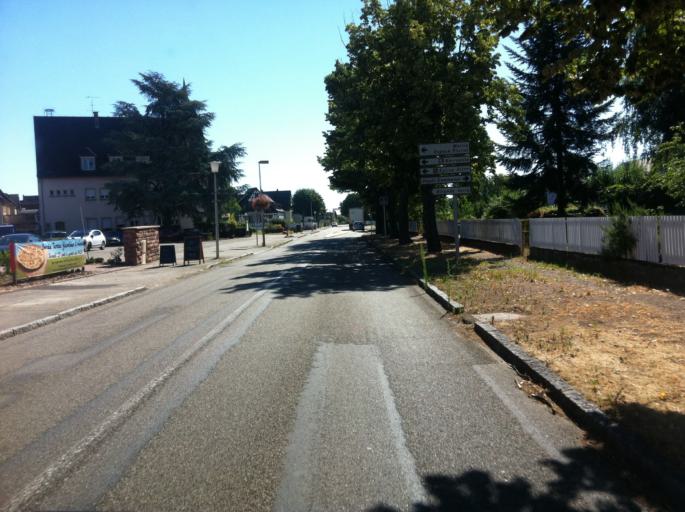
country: FR
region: Alsace
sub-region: Departement du Haut-Rhin
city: Sigolsheim
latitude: 48.1336
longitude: 7.2981
